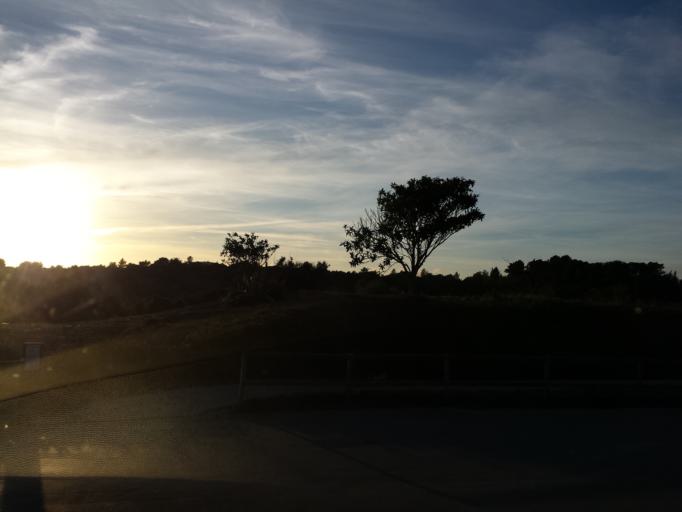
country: PT
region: Faro
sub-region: Lagos
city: Lagos
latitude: 37.1263
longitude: -8.6420
